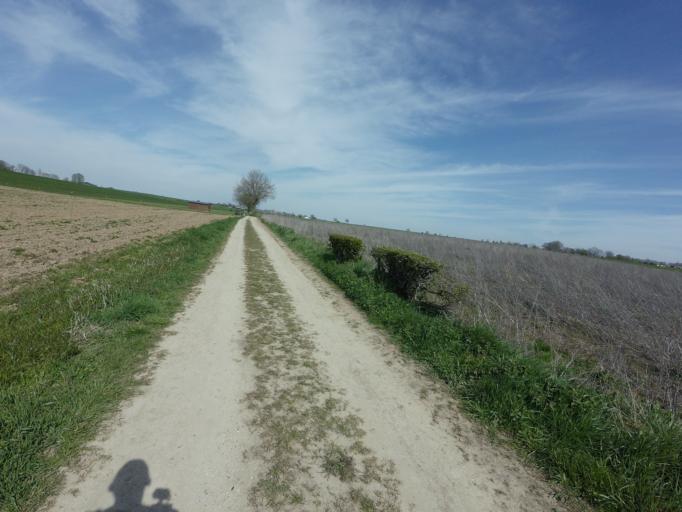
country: NL
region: Limburg
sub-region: Eijsden-Margraten
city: Margraten
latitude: 50.7899
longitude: 5.8209
